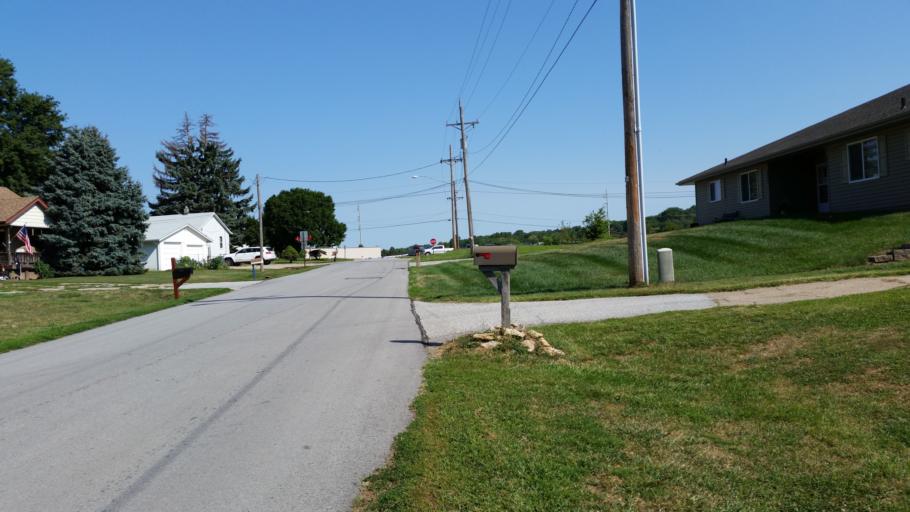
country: US
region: Nebraska
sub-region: Sarpy County
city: Bellevue
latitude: 41.1757
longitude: -95.9282
